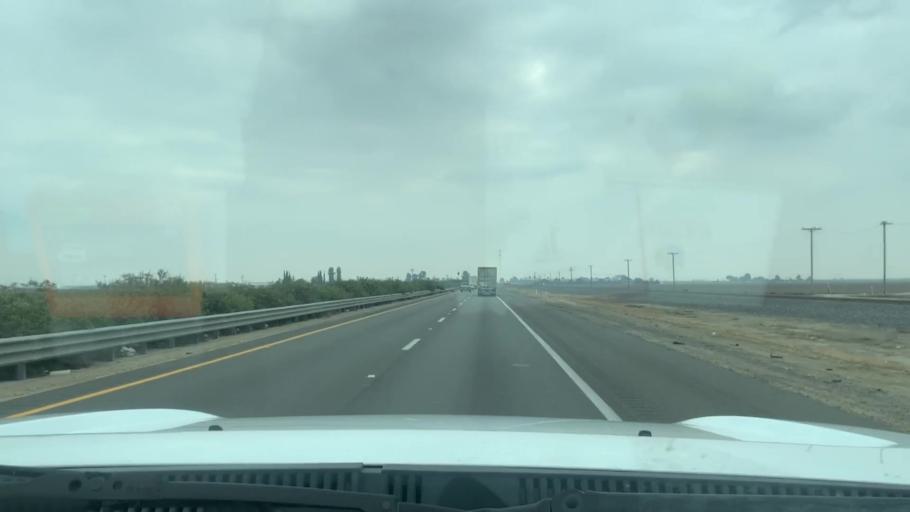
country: US
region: California
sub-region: Tulare County
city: Tipton
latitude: 36.0813
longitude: -119.3195
